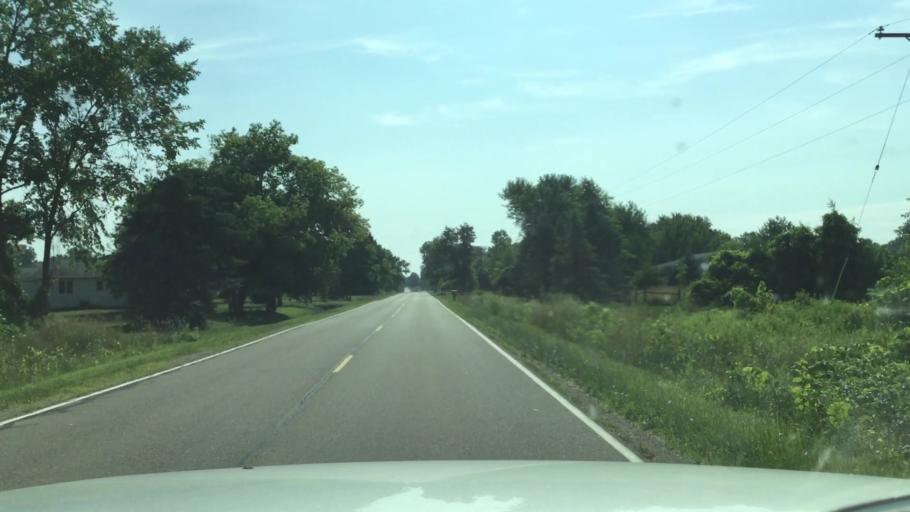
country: US
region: Michigan
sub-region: Genesee County
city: Flushing
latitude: 43.1335
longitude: -83.8194
